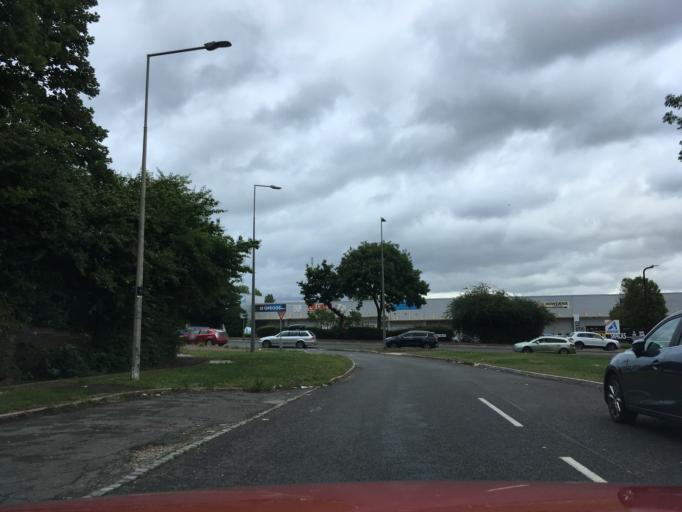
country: GB
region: England
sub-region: Buckinghamshire
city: Bletchley
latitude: 52.0109
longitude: -0.7480
